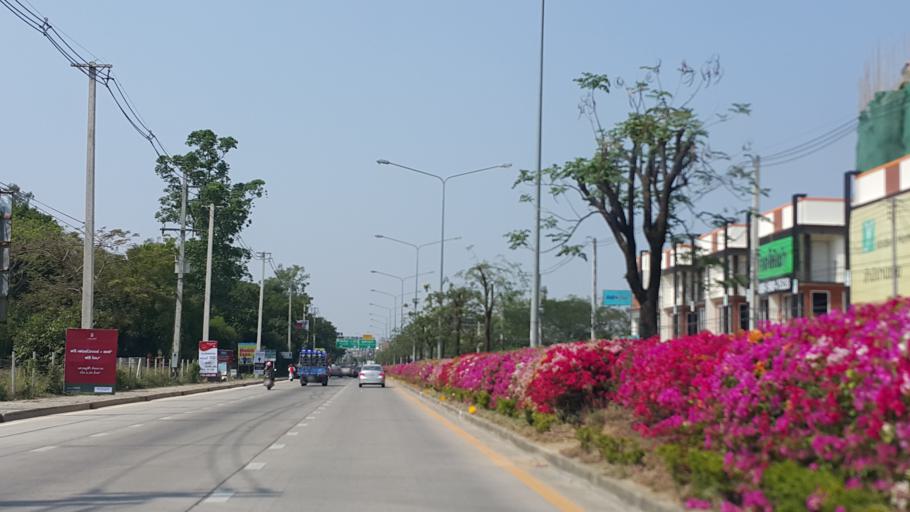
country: TH
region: Chiang Mai
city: San Sai
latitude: 18.8190
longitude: 99.0185
